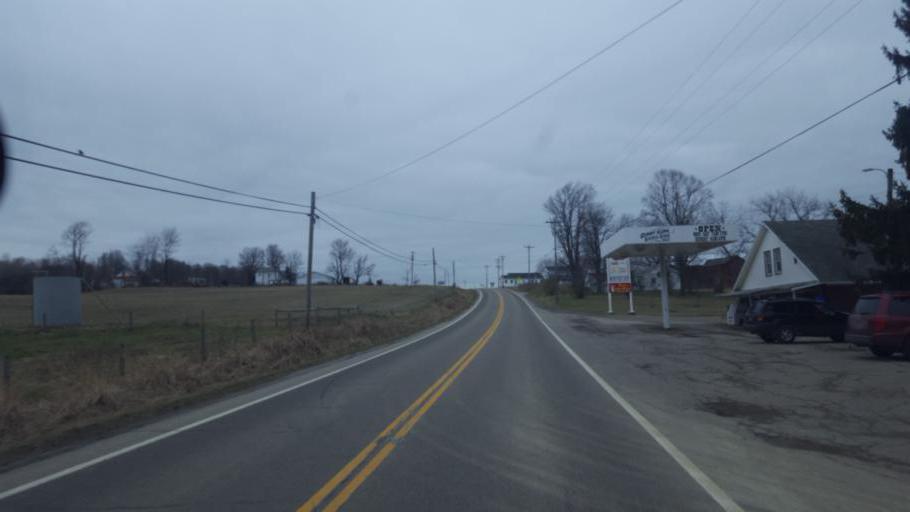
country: US
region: Ohio
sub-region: Wayne County
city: Shreve
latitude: 40.5857
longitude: -82.0627
